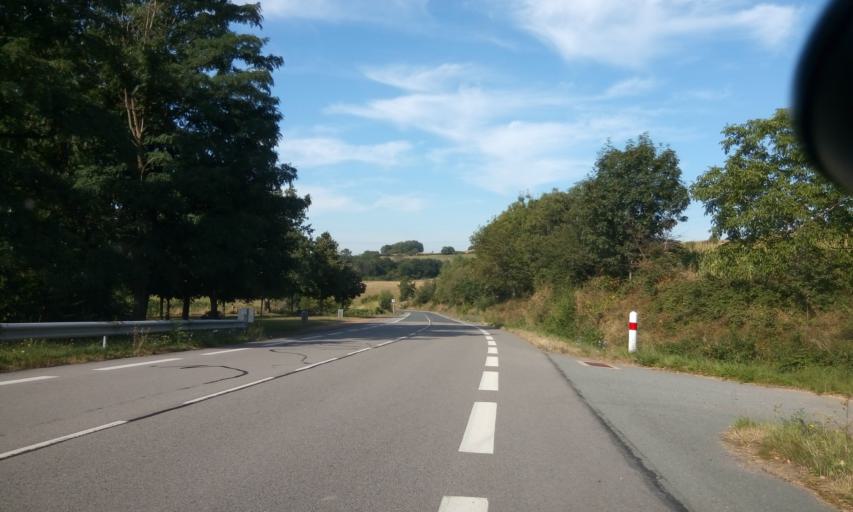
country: FR
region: Rhone-Alpes
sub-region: Departement du Rhone
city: Amplepuis
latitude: 45.9815
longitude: 4.3701
